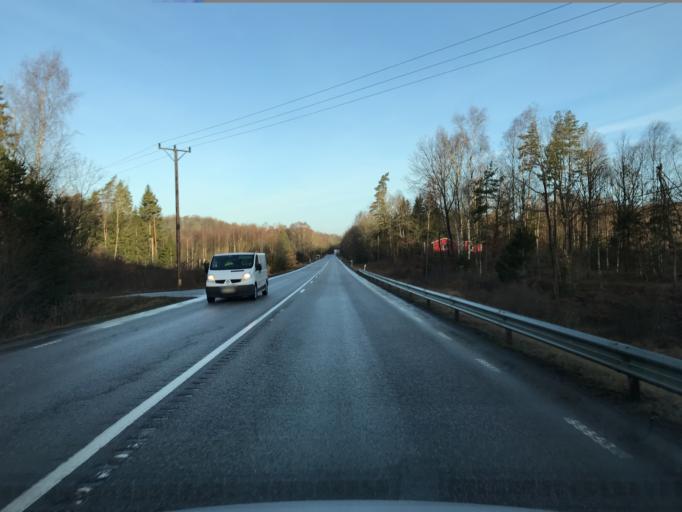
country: SE
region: Skane
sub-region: Hassleholms Kommun
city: Bjarnum
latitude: 56.2692
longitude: 13.7193
